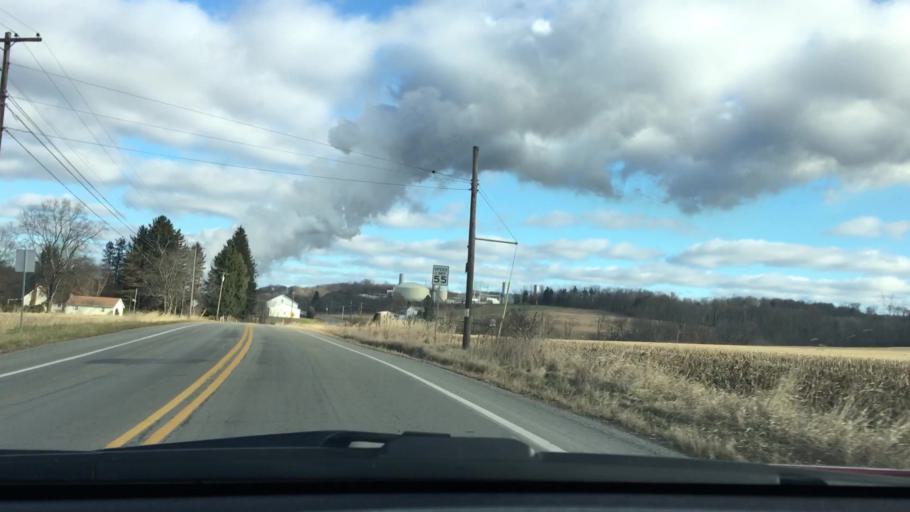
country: US
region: Pennsylvania
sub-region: Westmoreland County
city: Avonmore
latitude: 40.6305
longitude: -79.3611
